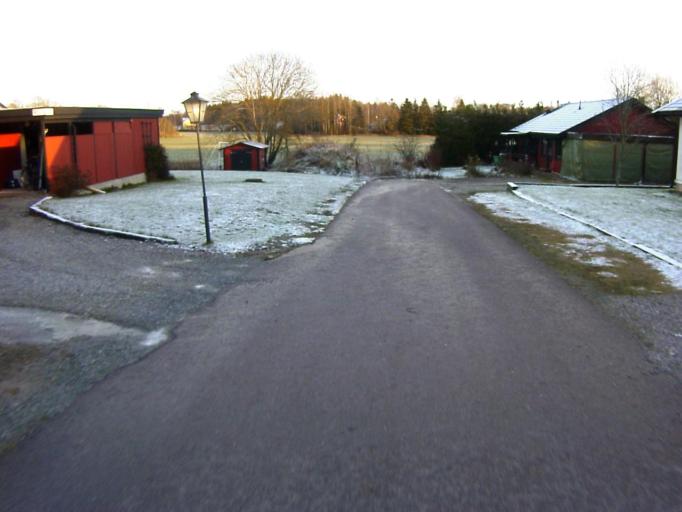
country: SE
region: Soedermanland
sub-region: Eskilstuna Kommun
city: Arla
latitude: 59.3201
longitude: 16.6020
